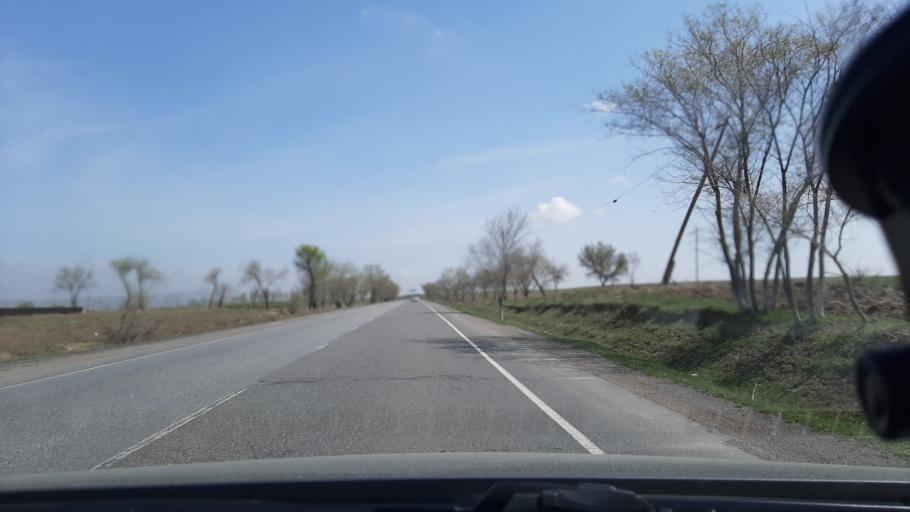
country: TJ
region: Viloyati Sughd
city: Shahriston
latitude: 39.7900
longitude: 68.8723
